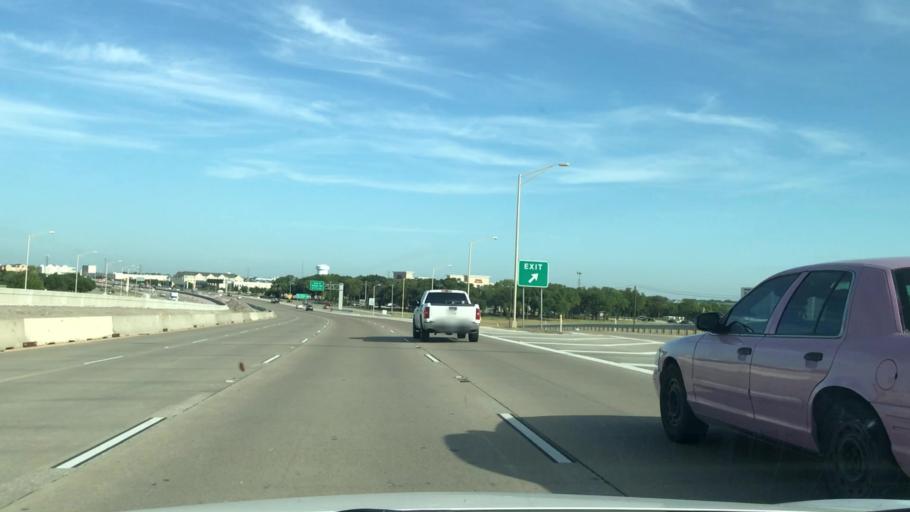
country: US
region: Texas
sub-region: Collin County
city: Plano
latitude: 32.9979
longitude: -96.6714
